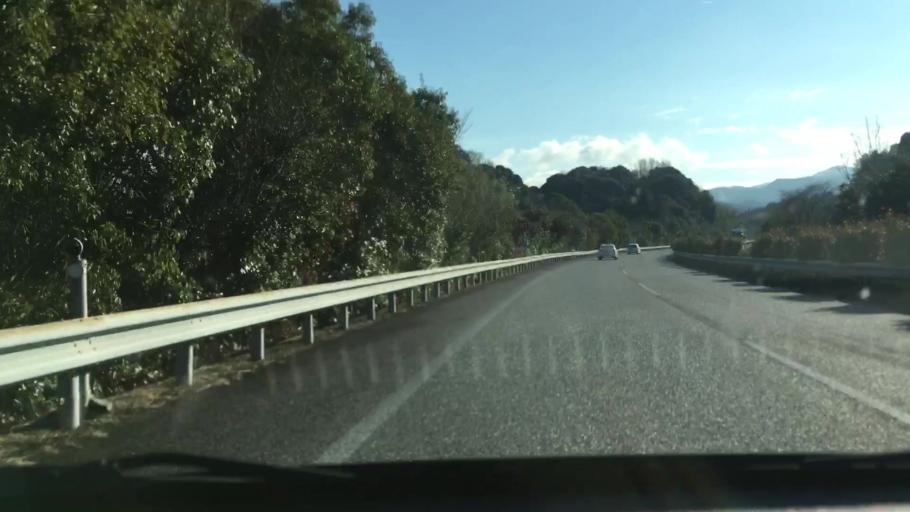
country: JP
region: Kumamoto
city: Hitoyoshi
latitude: 32.1951
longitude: 130.7779
